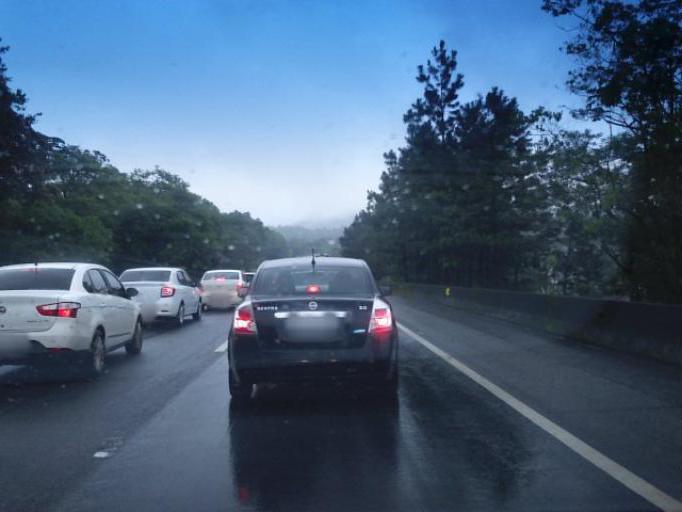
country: BR
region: Santa Catarina
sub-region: Joinville
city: Joinville
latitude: -26.1535
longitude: -48.9084
